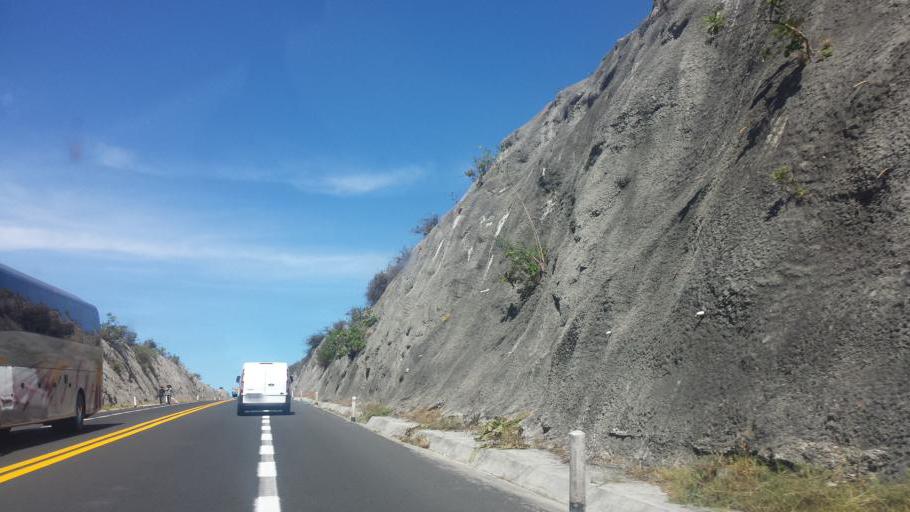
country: MX
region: Puebla
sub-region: San Jose Miahuatlan
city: San Pedro Tetitlan
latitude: 17.9983
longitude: -97.3548
